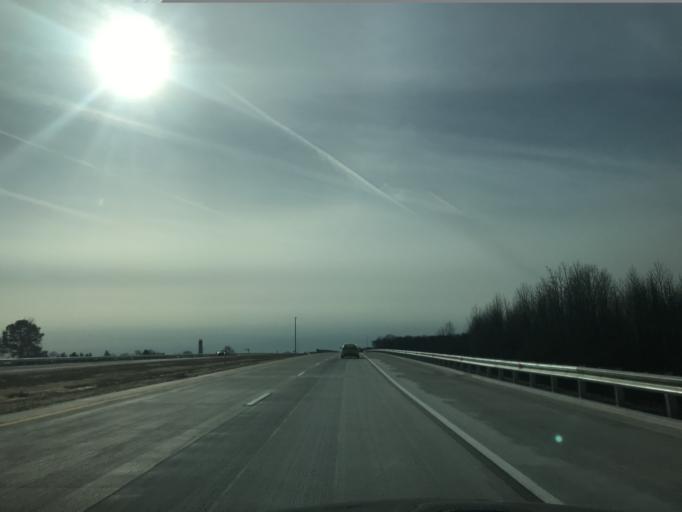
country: US
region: Delaware
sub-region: New Castle County
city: Middletown
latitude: 39.5099
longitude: -75.6923
